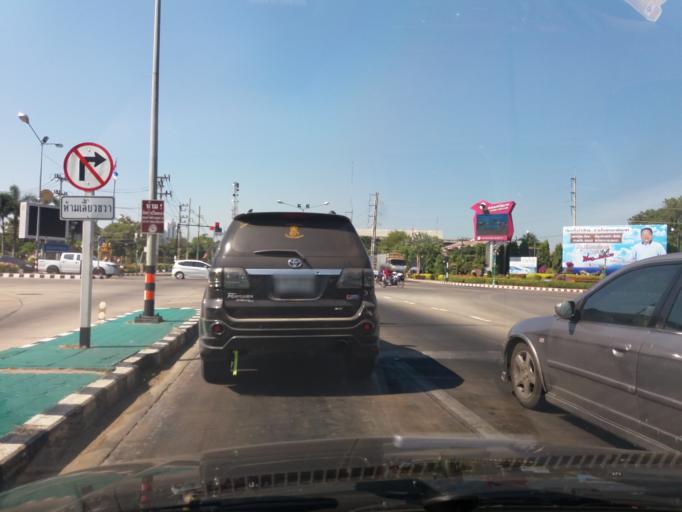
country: TH
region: Chai Nat
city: Chai Nat
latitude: 15.1888
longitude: 100.1305
